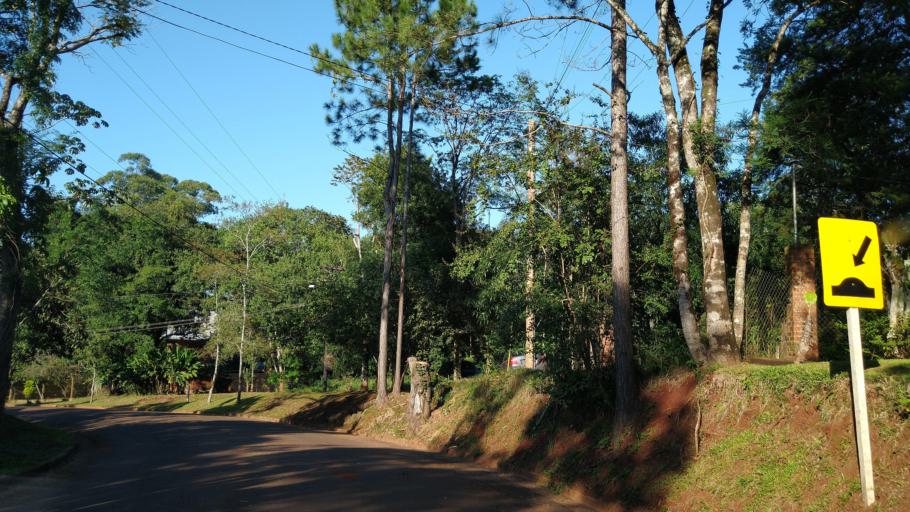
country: AR
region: Misiones
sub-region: Departamento de Montecarlo
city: Montecarlo
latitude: -26.5592
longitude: -54.7770
